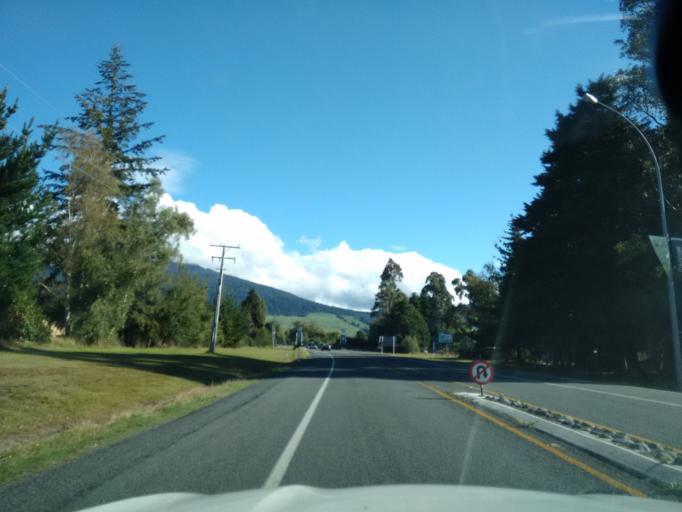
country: NZ
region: Waikato
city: Turangi
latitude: -38.9917
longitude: 175.8091
